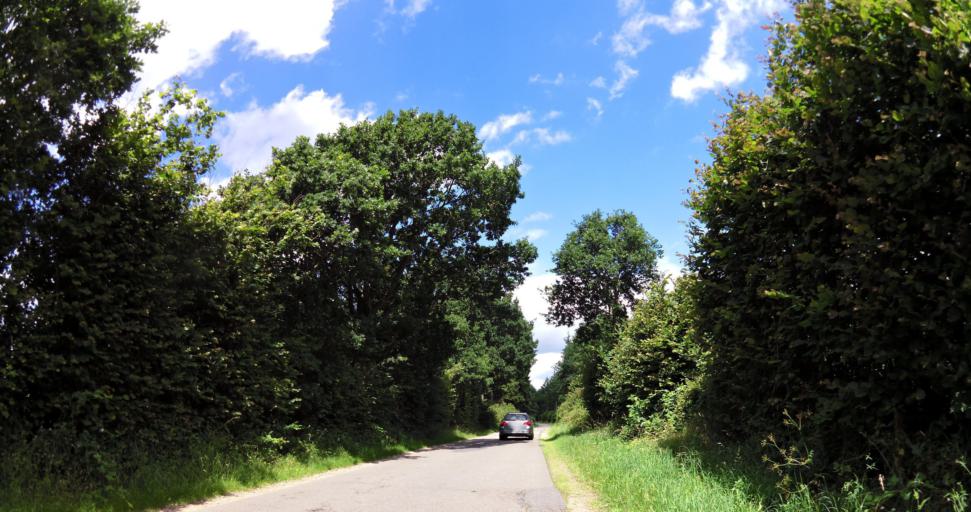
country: DE
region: Schleswig-Holstein
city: Brodersby
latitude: 54.5055
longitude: 9.7222
